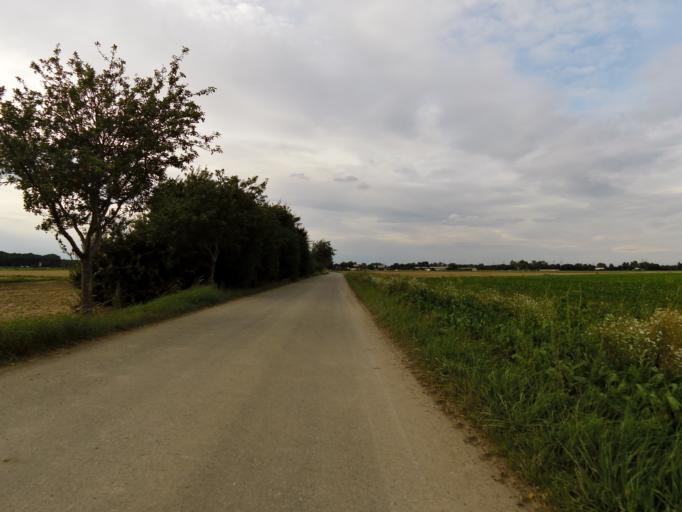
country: DE
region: Rheinland-Pfalz
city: Worms
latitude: 49.6265
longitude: 8.4038
